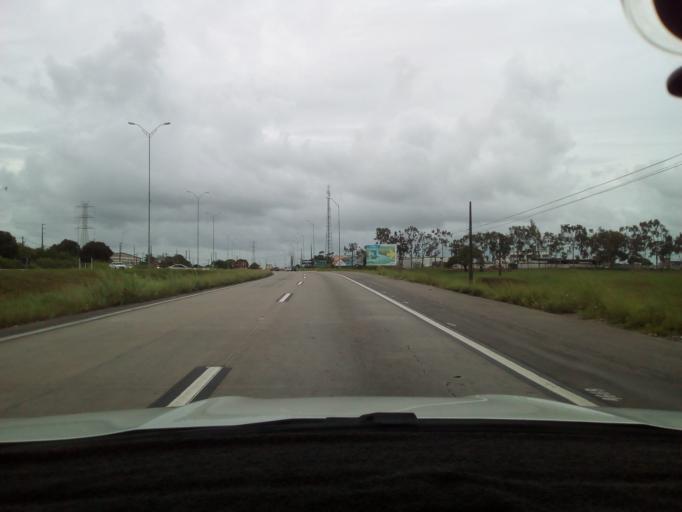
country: BR
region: Paraiba
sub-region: Conde
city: Conde
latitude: -7.2622
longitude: -34.9361
